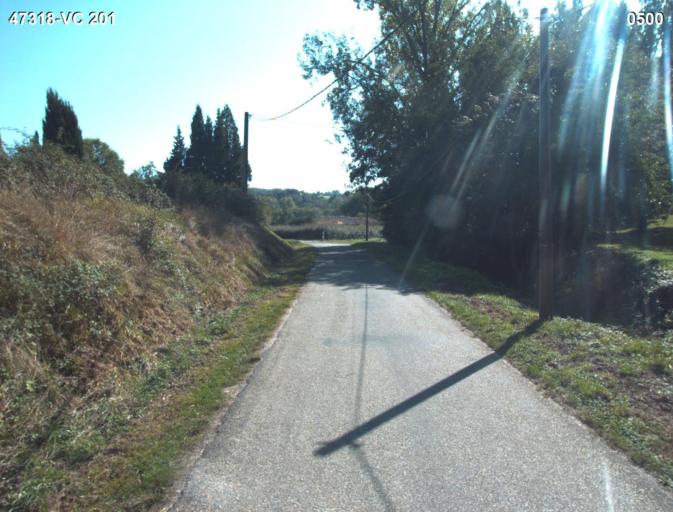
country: FR
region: Aquitaine
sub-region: Departement du Lot-et-Garonne
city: Vianne
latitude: 44.2022
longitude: 0.3193
